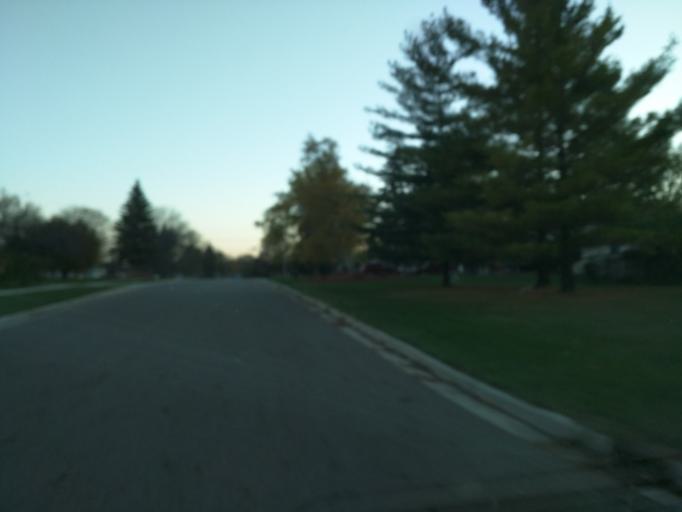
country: US
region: Michigan
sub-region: Eaton County
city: Waverly
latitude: 42.7301
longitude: -84.6086
